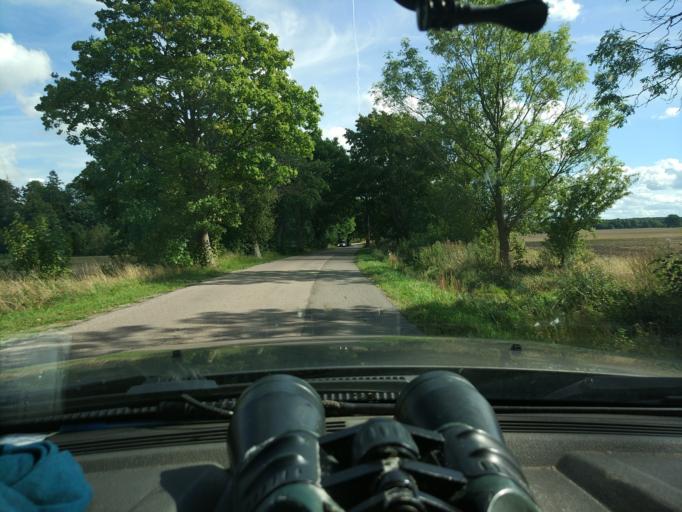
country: PL
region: Pomeranian Voivodeship
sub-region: Powiat wejherowski
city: Choczewo
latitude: 54.7418
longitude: 17.8136
